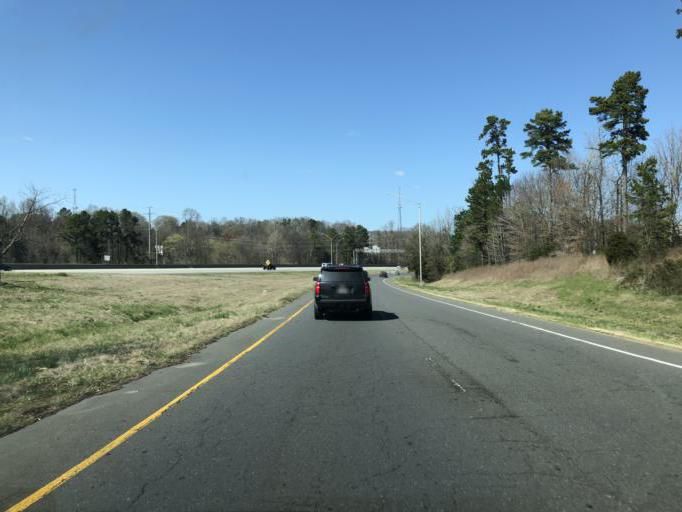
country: US
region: North Carolina
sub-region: Cabarrus County
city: Harrisburg
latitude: 35.3126
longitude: -80.7566
